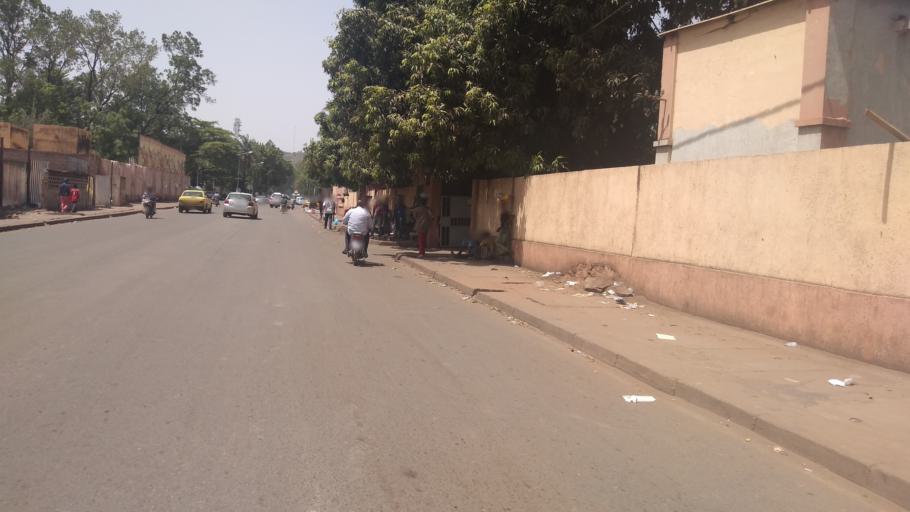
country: ML
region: Bamako
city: Bamako
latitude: 12.6452
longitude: -8.0020
